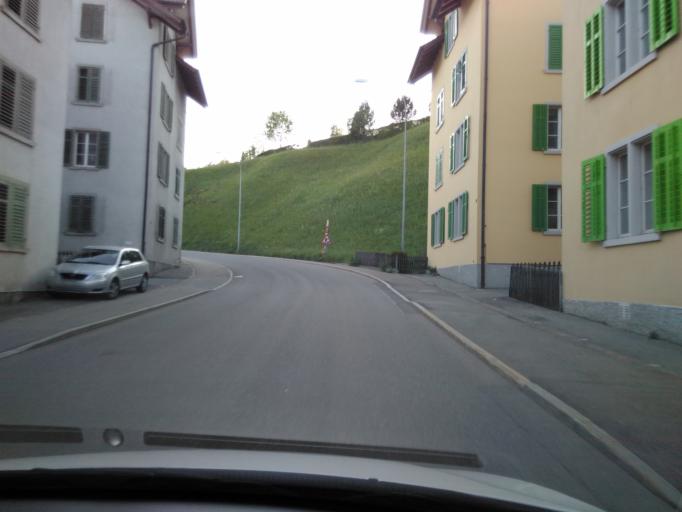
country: CH
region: Zurich
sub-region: Bezirk Hinwil
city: Wald
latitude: 47.2767
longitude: 8.9103
